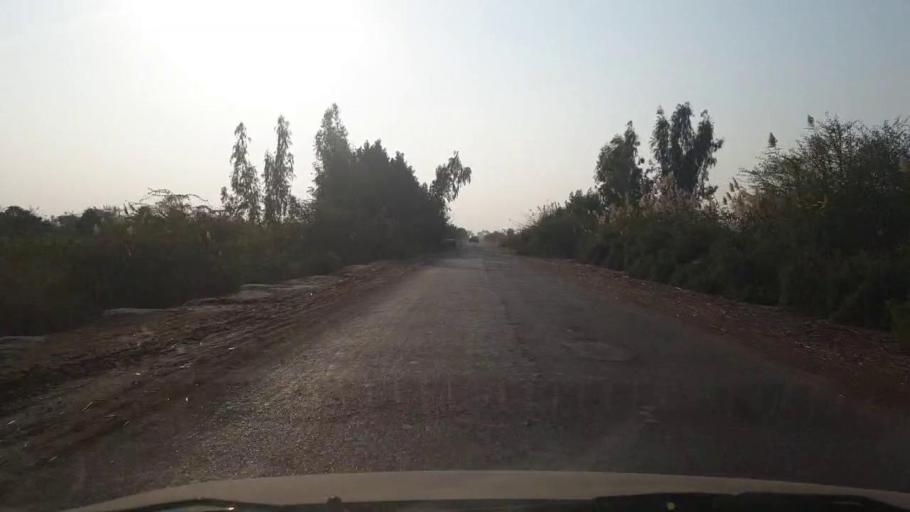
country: PK
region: Sindh
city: Mirwah Gorchani
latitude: 25.3683
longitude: 69.1750
